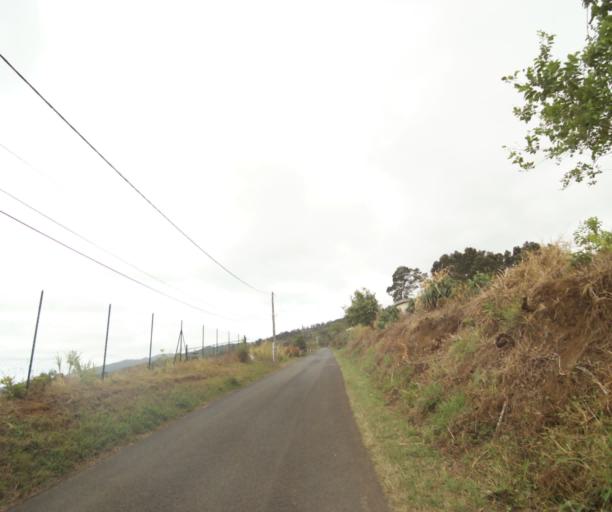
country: RE
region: Reunion
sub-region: Reunion
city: Saint-Paul
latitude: -21.0113
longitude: 55.3385
